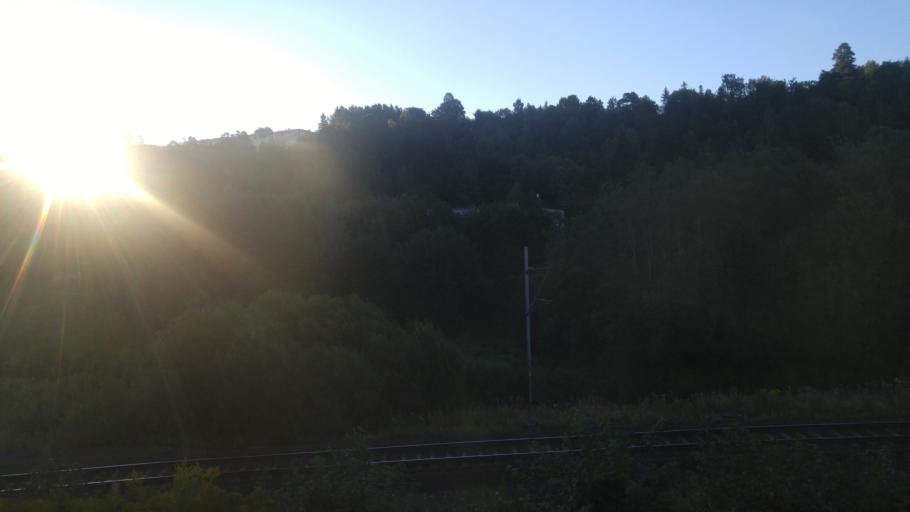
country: NO
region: Oslo
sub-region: Oslo
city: Oslo
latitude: 59.9145
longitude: 10.8281
